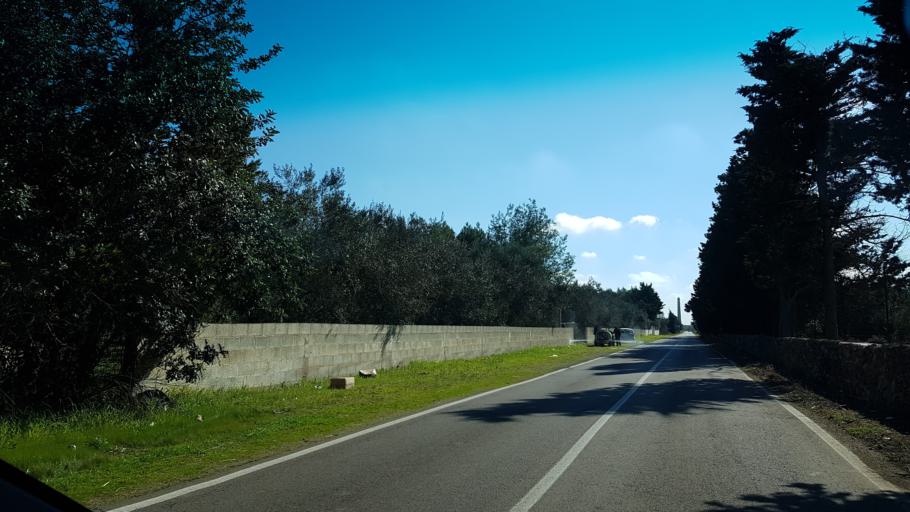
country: IT
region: Apulia
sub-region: Provincia di Lecce
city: Campi Salentina
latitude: 40.4112
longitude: 18.0141
